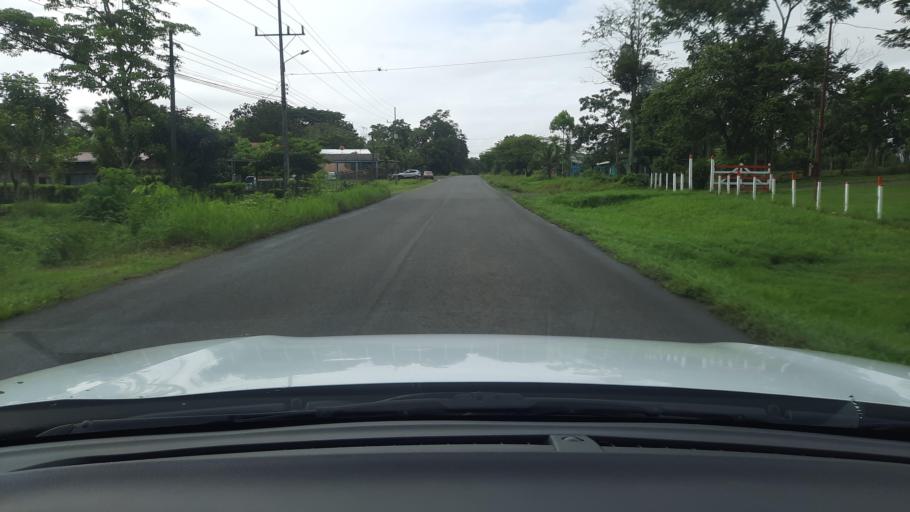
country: CR
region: Alajuela
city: San Jose
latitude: 10.9512
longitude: -85.1238
